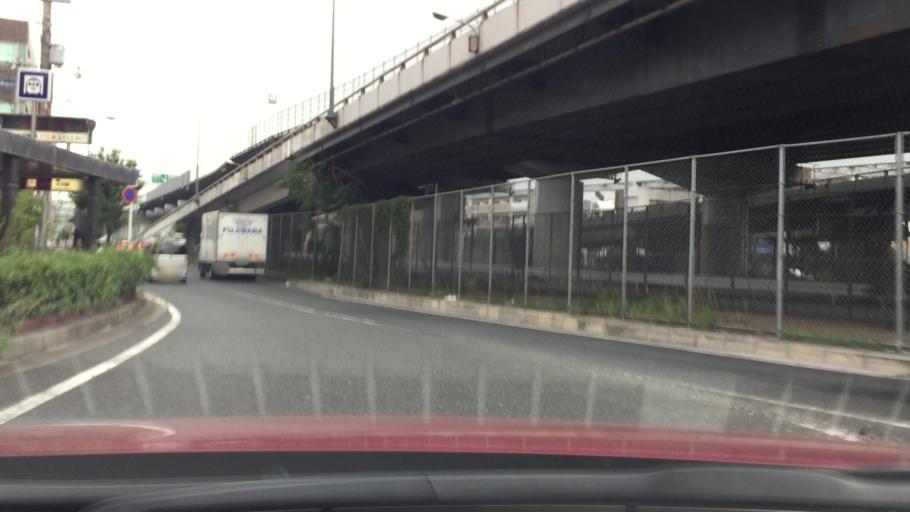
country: JP
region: Osaka
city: Kadoma
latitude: 34.7495
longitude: 135.5779
